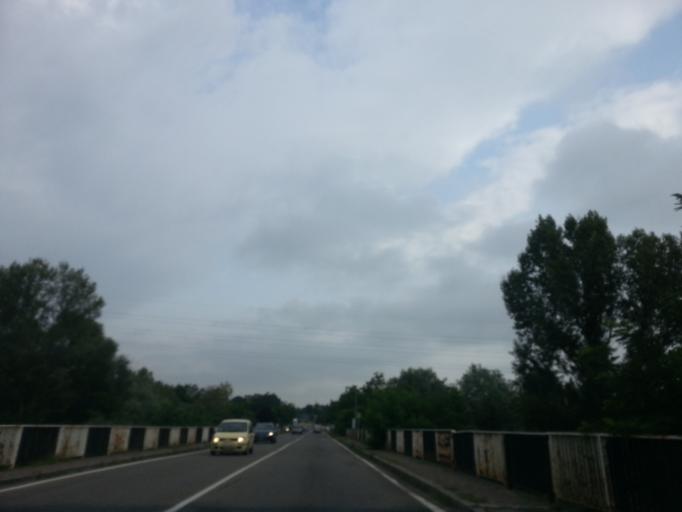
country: IT
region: Emilia-Romagna
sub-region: Provincia di Reggio Emilia
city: Pratissolo
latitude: 44.5950
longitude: 10.6775
